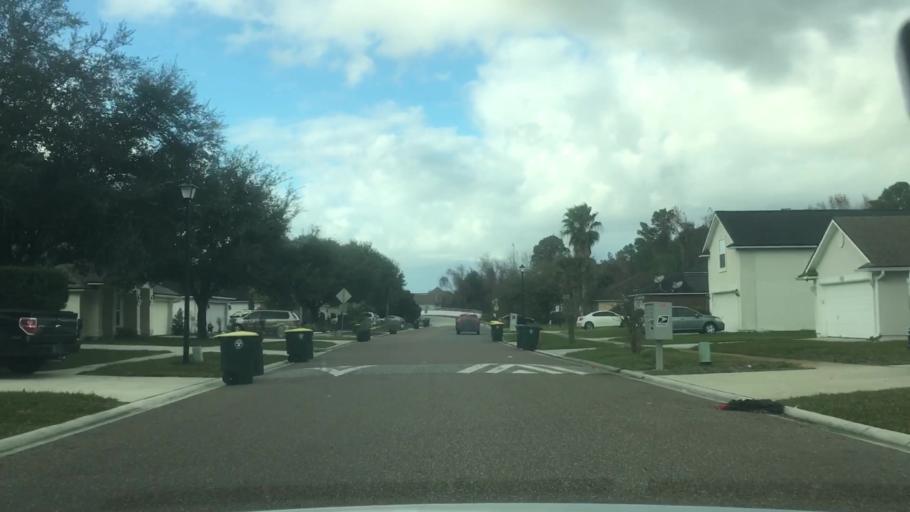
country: US
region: Florida
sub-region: Duval County
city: Neptune Beach
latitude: 30.3048
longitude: -81.5037
